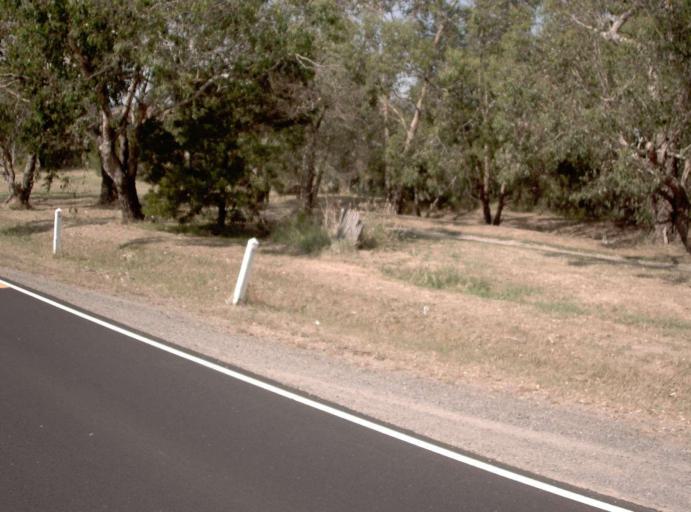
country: AU
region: Victoria
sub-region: Yarra Ranges
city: Lysterfield
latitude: -37.9161
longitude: 145.2713
